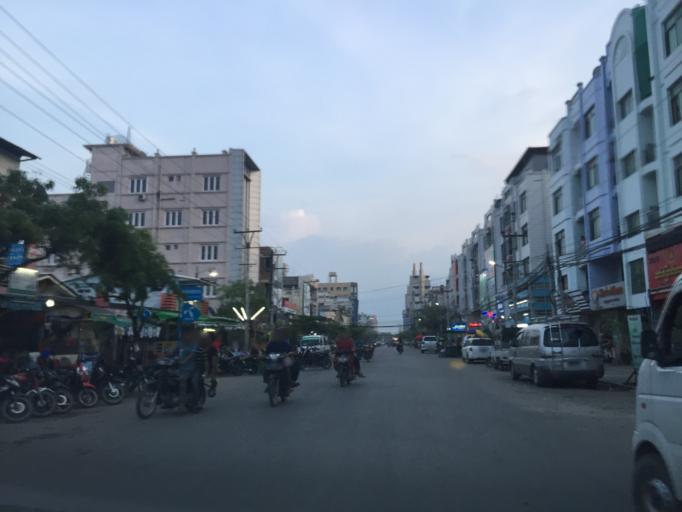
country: MM
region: Mandalay
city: Mandalay
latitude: 21.9749
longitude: 96.0884
